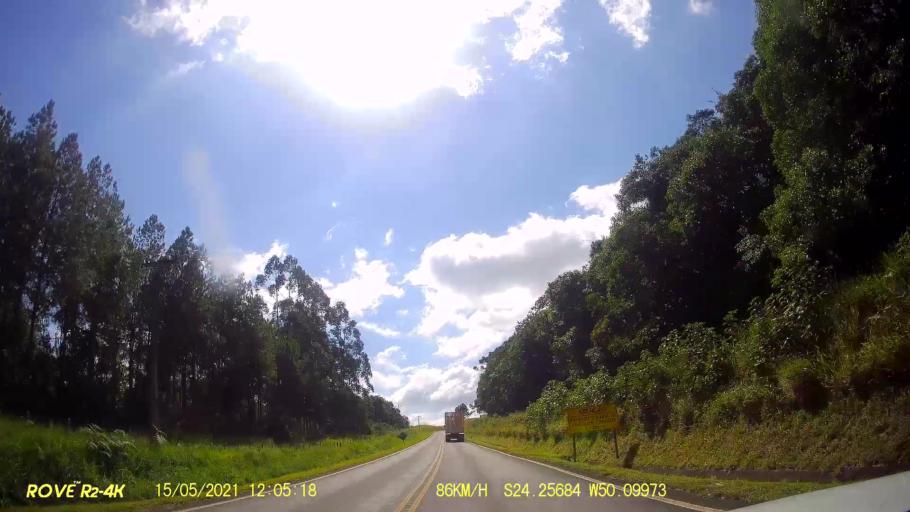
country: BR
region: Parana
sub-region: Pirai Do Sul
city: Pirai do Sul
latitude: -24.2567
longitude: -50.0998
